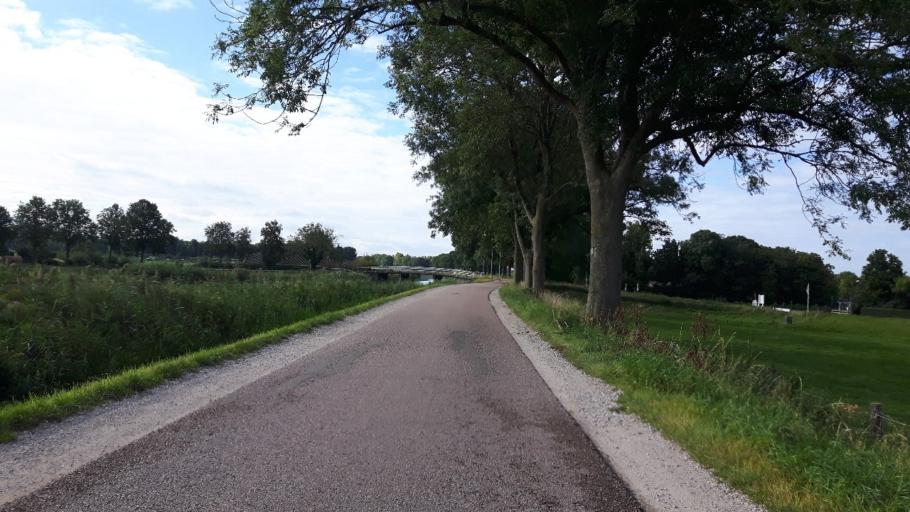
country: NL
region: North Holland
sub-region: Gemeente Purmerend
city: Purmerend
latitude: 52.5349
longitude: 4.9605
